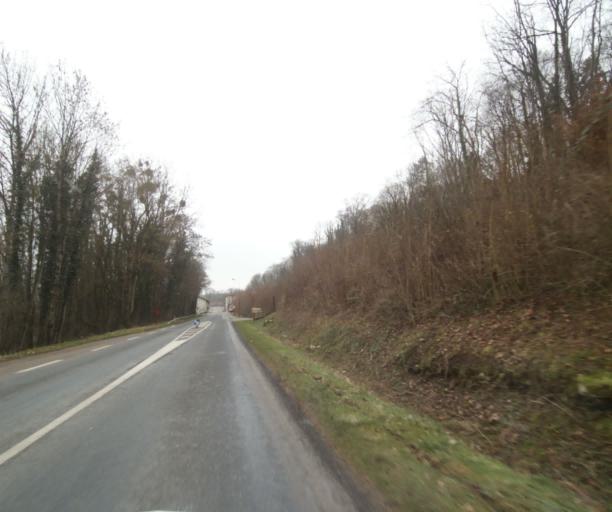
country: FR
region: Champagne-Ardenne
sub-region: Departement de la Haute-Marne
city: Bienville
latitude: 48.5515
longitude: 5.0696
